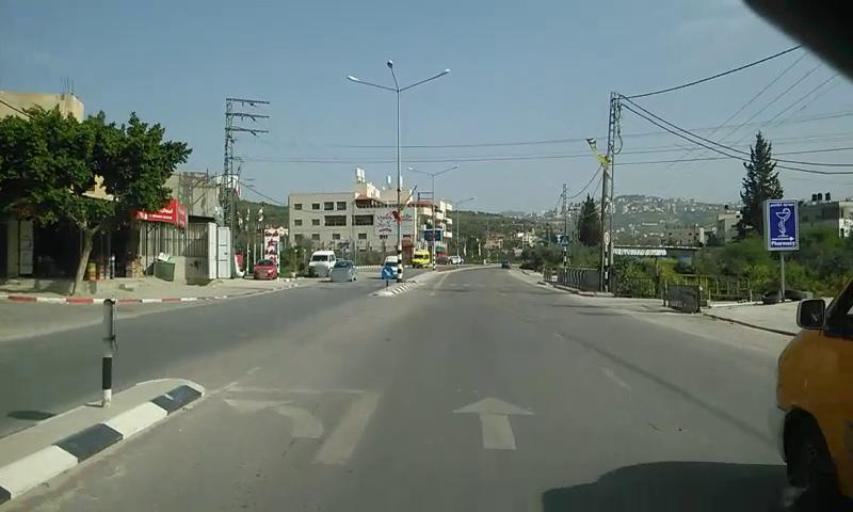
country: PS
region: West Bank
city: Dayr Sharaf
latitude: 32.2511
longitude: 35.1883
